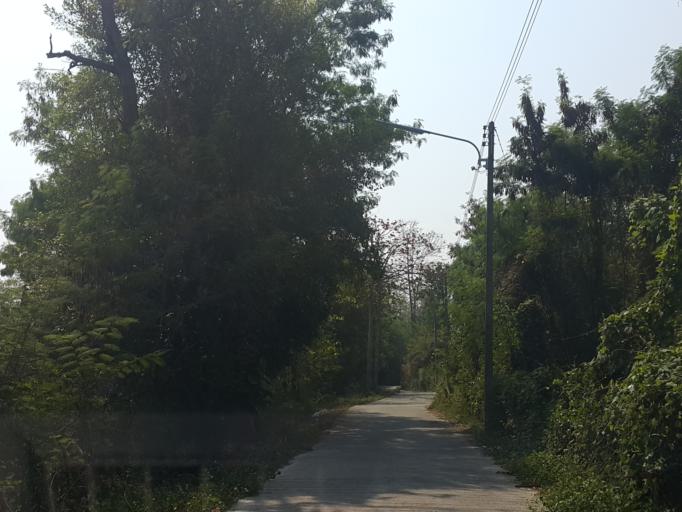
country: TH
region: Chiang Mai
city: San Kamphaeng
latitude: 18.7568
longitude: 99.1376
